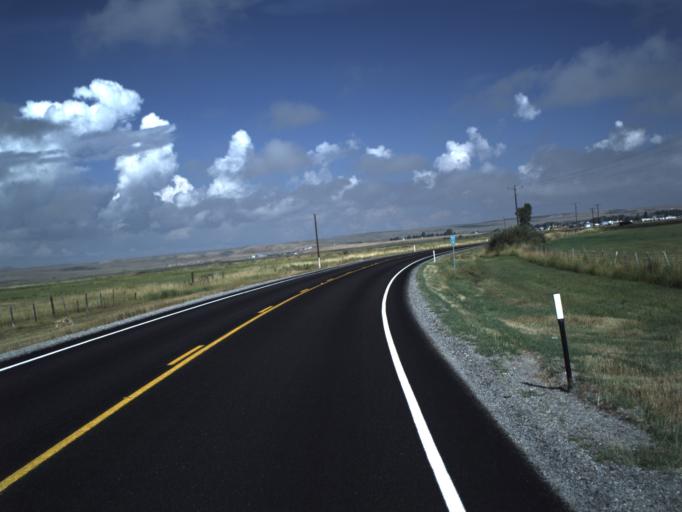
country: US
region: Utah
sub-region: Rich County
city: Randolph
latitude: 41.6404
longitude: -111.1825
